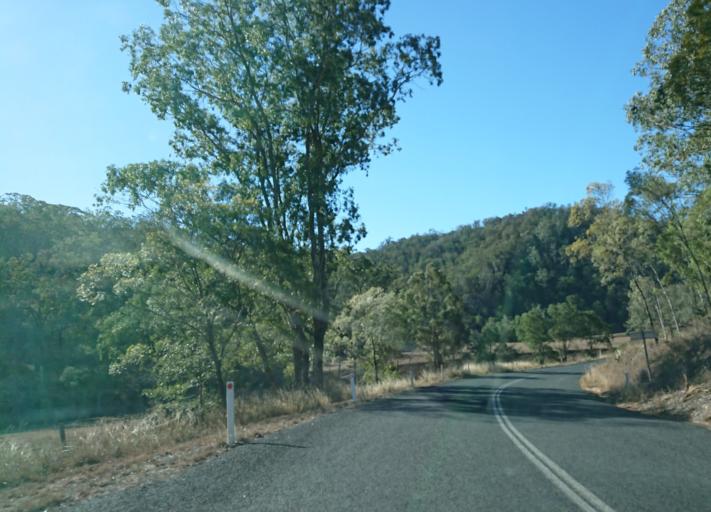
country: AU
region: Queensland
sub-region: Toowoomba
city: Top Camp
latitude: -27.7539
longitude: 152.0813
